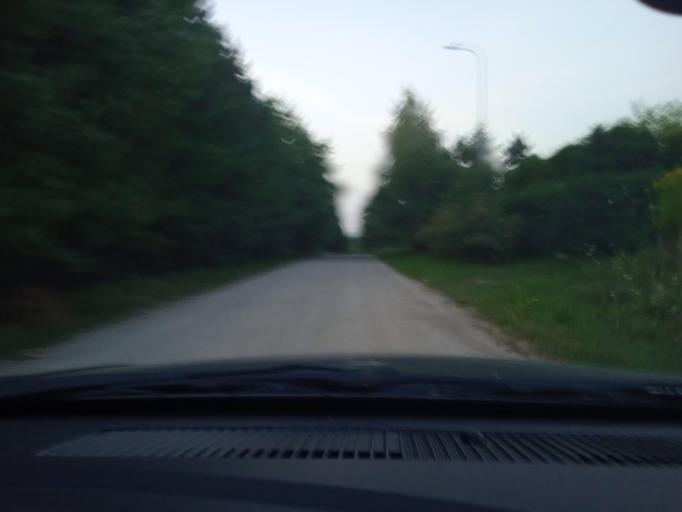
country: PL
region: Masovian Voivodeship
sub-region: Powiat nowodworski
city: Pomiechowek
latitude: 52.4882
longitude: 20.7038
